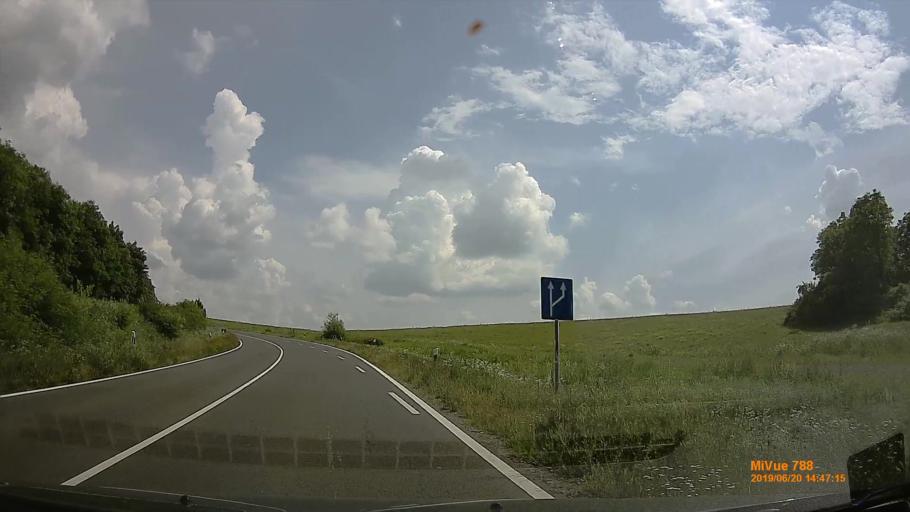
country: HU
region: Baranya
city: Kozarmisleny
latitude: 46.0243
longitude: 18.2806
